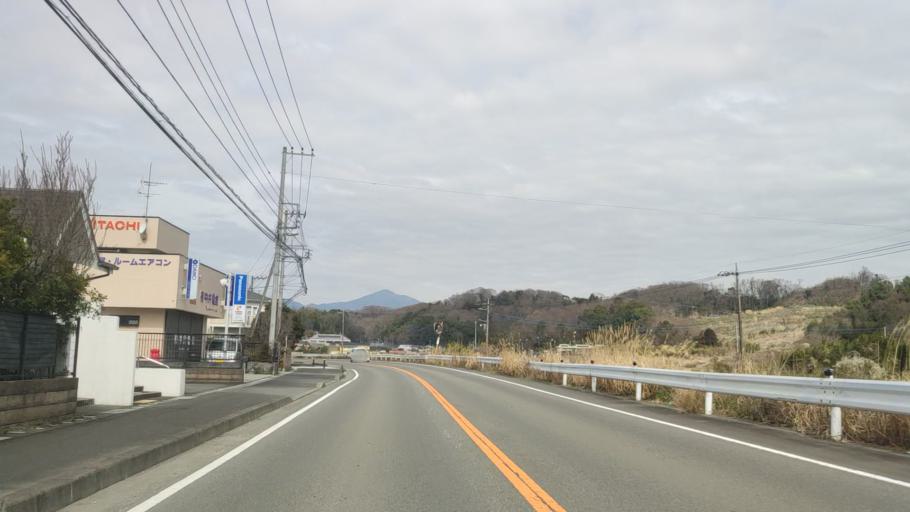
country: JP
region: Kanagawa
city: Ninomiya
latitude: 35.3260
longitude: 139.2192
